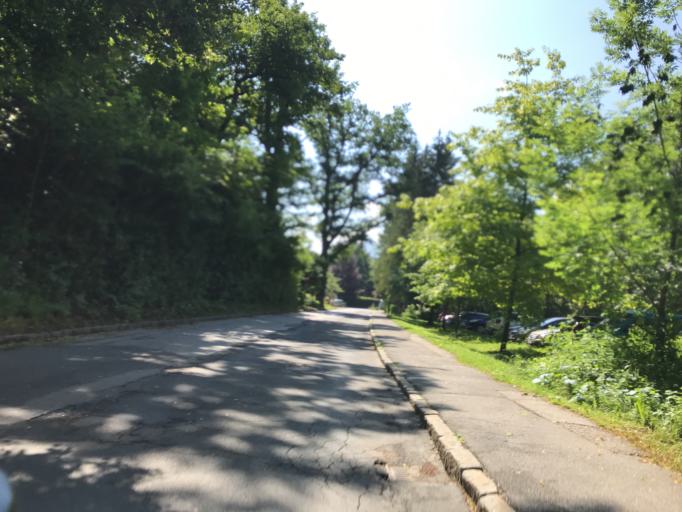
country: AT
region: Carinthia
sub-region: Villach Stadt
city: Villach
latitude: 46.5923
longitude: 13.8263
